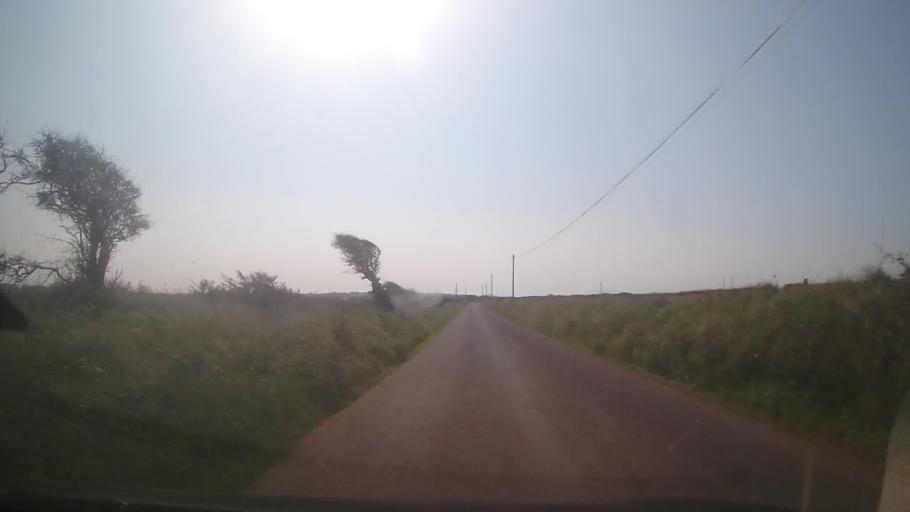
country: GB
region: Wales
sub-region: Pembrokeshire
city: Saint David's
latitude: 51.9061
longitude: -5.2427
